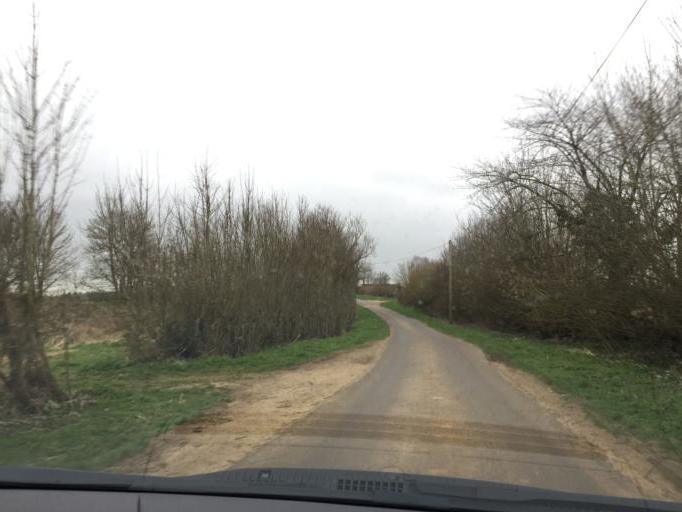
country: GB
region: England
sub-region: Oxfordshire
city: Deddington
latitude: 51.9358
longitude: -1.3706
